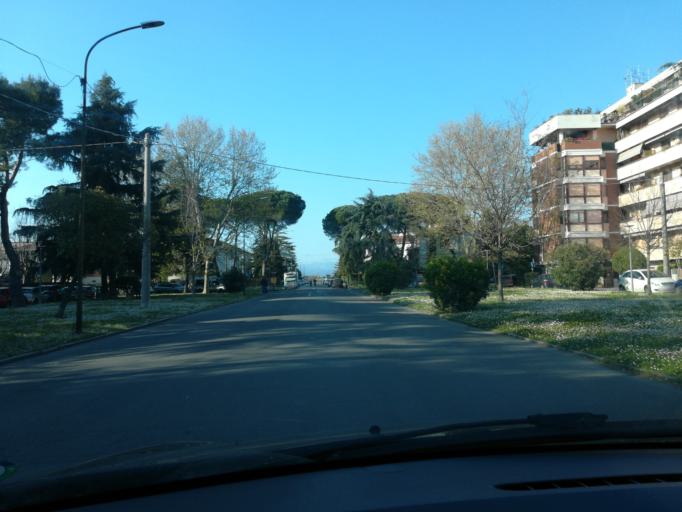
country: IT
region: Tuscany
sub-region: Province of Pisa
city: Pisa
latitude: 43.7323
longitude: 10.4030
